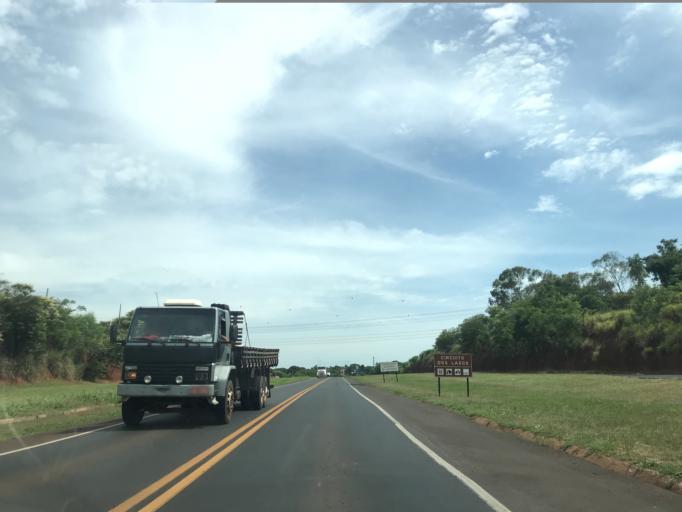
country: BR
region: Sao Paulo
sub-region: Nova Granada
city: Nova Granada
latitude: -20.3004
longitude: -49.2065
